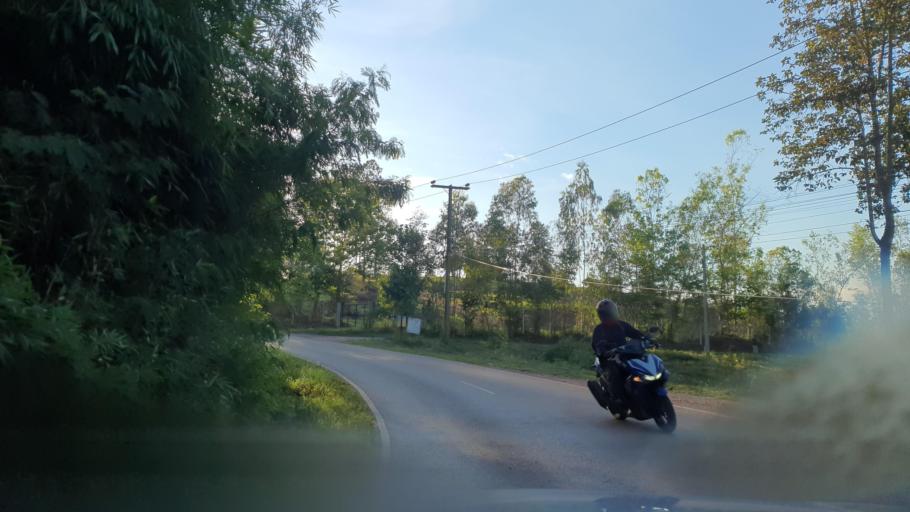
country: TH
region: Chiang Mai
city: Mae On
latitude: 18.8444
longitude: 99.2790
